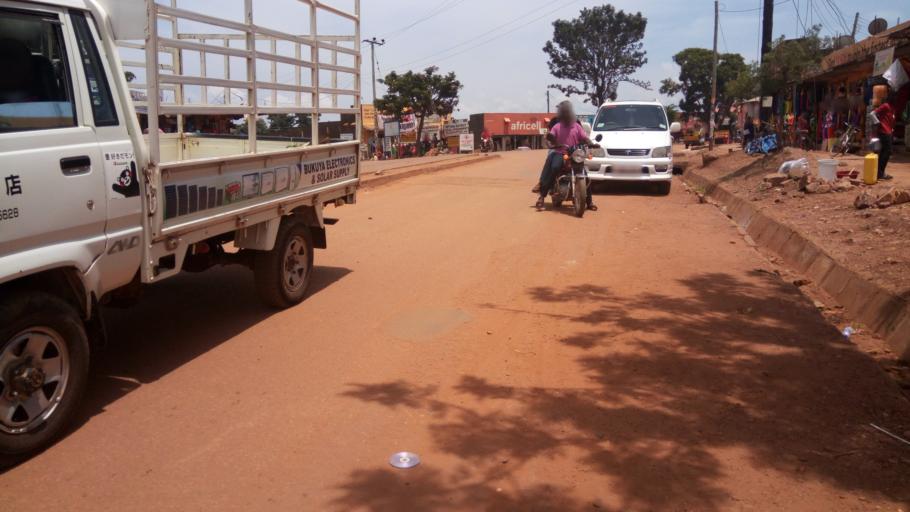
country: UG
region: Central Region
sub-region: Mityana District
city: Mityana
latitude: 0.3993
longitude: 32.0438
